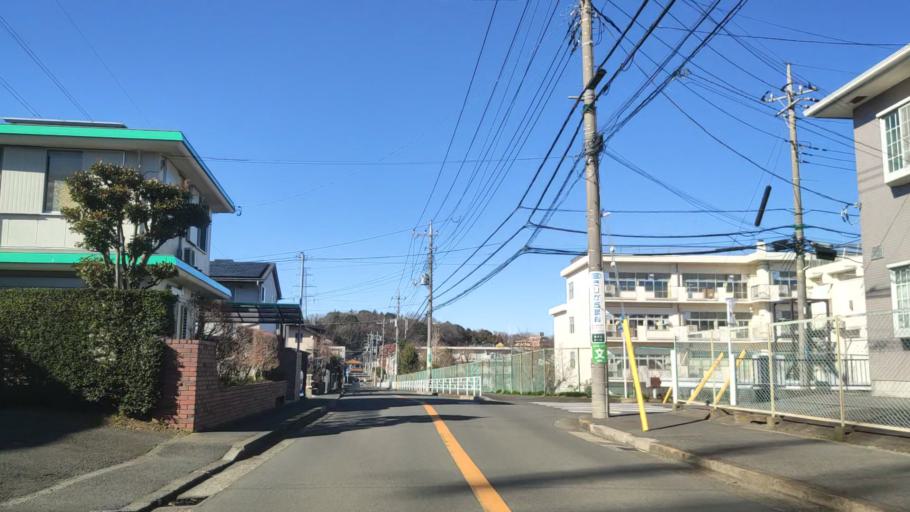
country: JP
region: Kanagawa
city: Minami-rinkan
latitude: 35.5098
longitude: 139.4989
